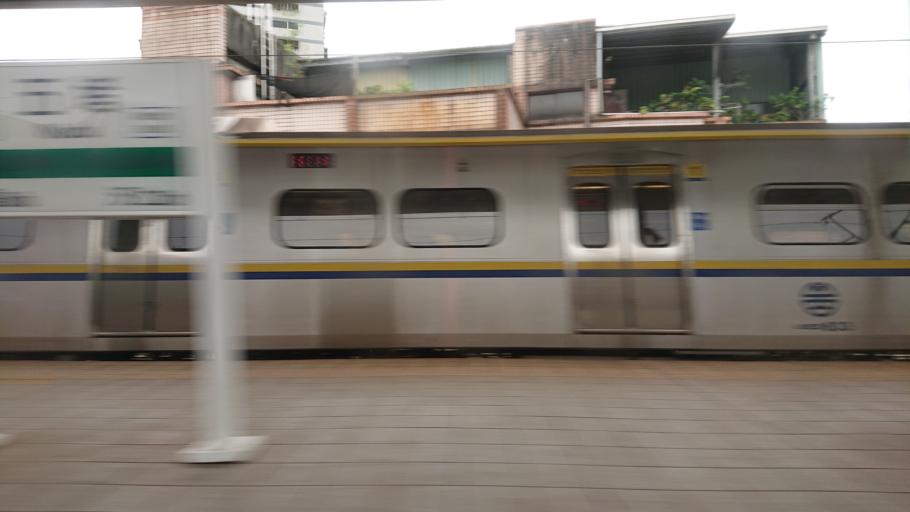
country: TW
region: Taiwan
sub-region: Keelung
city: Keelung
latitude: 25.0775
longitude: 121.6672
